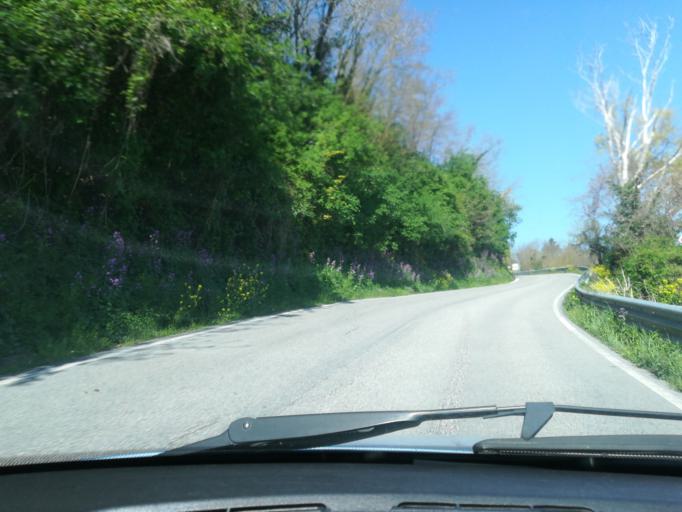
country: IT
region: The Marches
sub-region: Provincia di Macerata
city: Cingoli
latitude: 43.3765
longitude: 13.2205
